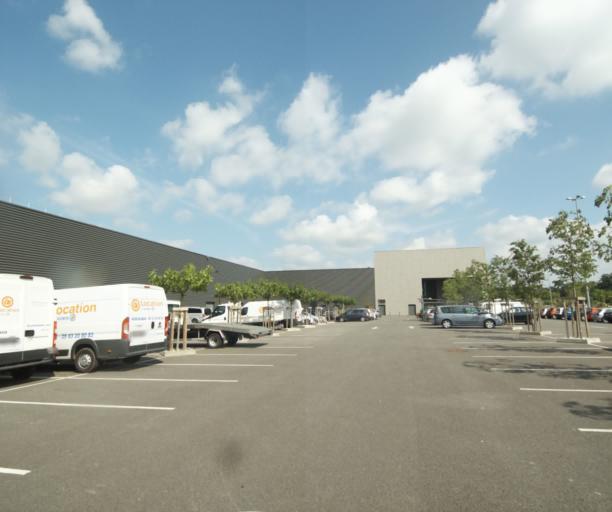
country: FR
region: Midi-Pyrenees
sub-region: Departement du Tarn-et-Garonne
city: Montauban
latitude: 44.0381
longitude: 1.3779
